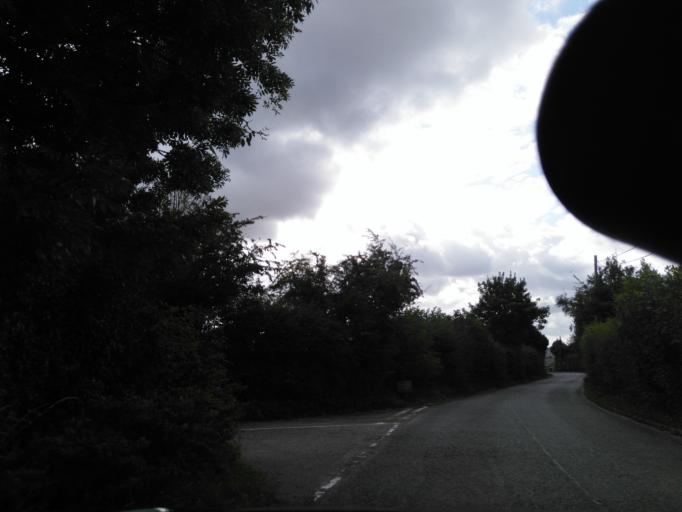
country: GB
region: England
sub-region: Dorset
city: Shaftesbury
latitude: 50.9968
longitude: -2.1759
